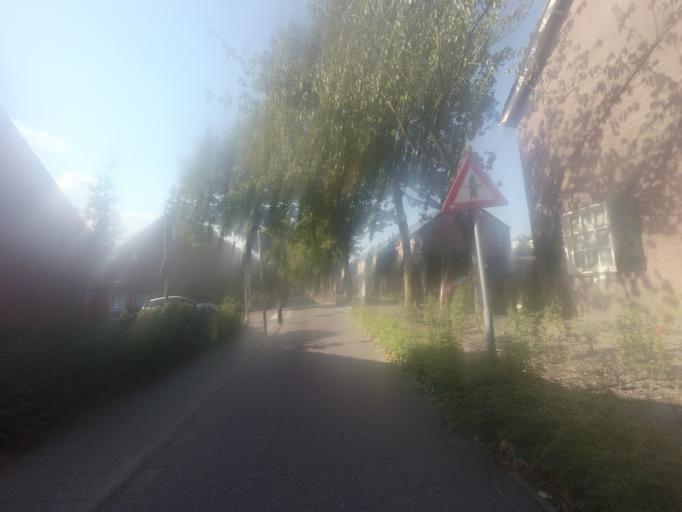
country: NL
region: North Brabant
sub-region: Gemeente Goirle
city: Goirle
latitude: 51.5275
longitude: 5.0503
